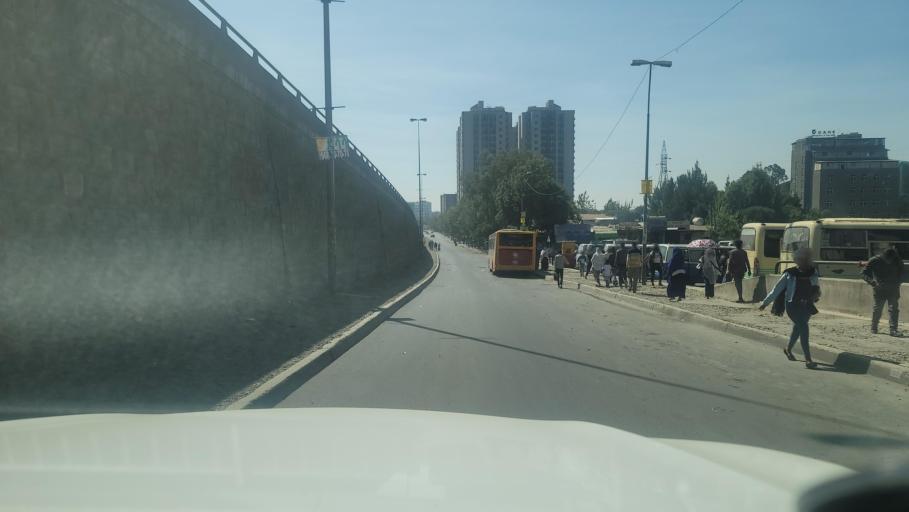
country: ET
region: Adis Abeba
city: Addis Ababa
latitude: 9.0181
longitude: 38.8018
